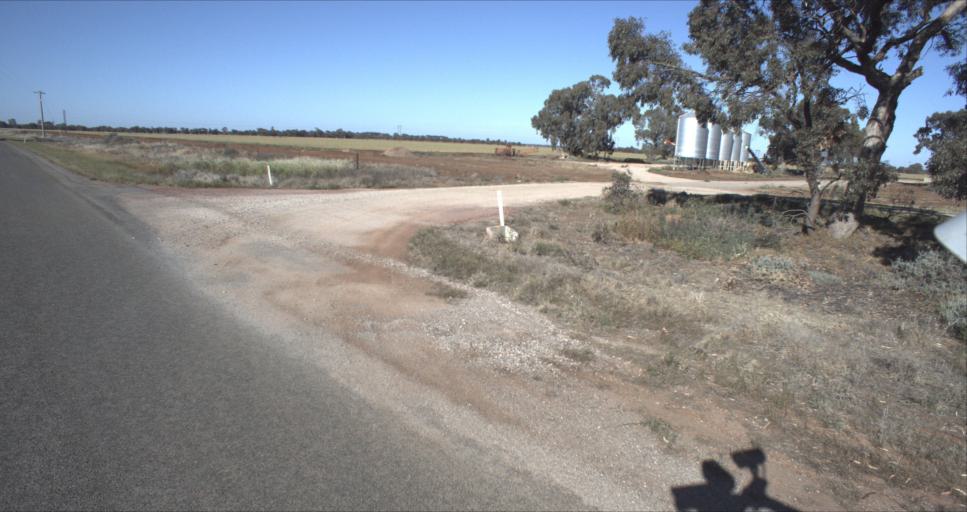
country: AU
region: New South Wales
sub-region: Leeton
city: Leeton
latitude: -34.5555
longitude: 146.2665
